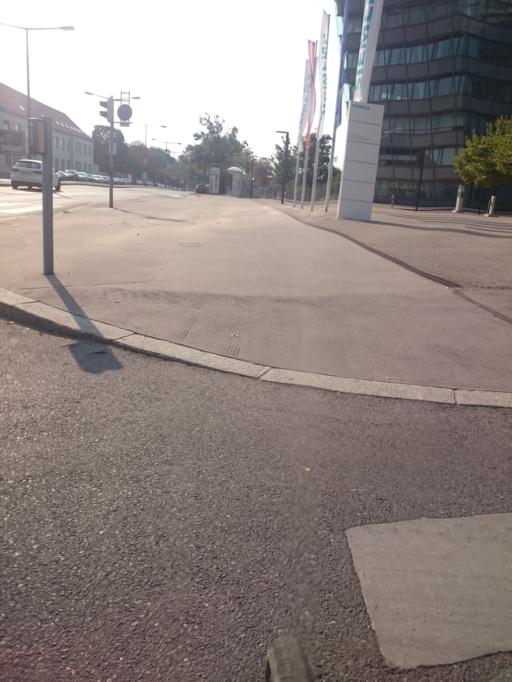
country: AT
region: Lower Austria
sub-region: Politischer Bezirk Wien-Umgebung
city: Gerasdorf bei Wien
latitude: 48.2699
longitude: 16.4225
